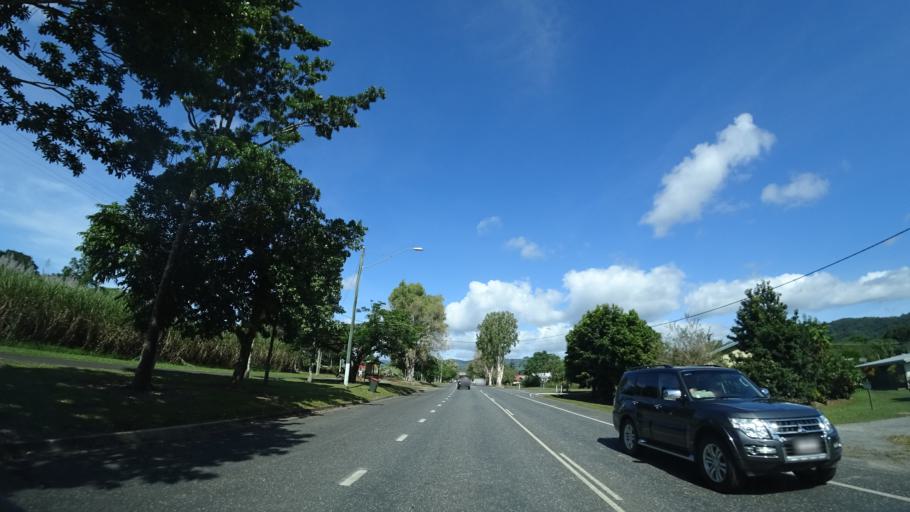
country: AU
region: Queensland
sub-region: Cairns
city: Port Douglas
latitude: -16.4718
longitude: 145.3737
